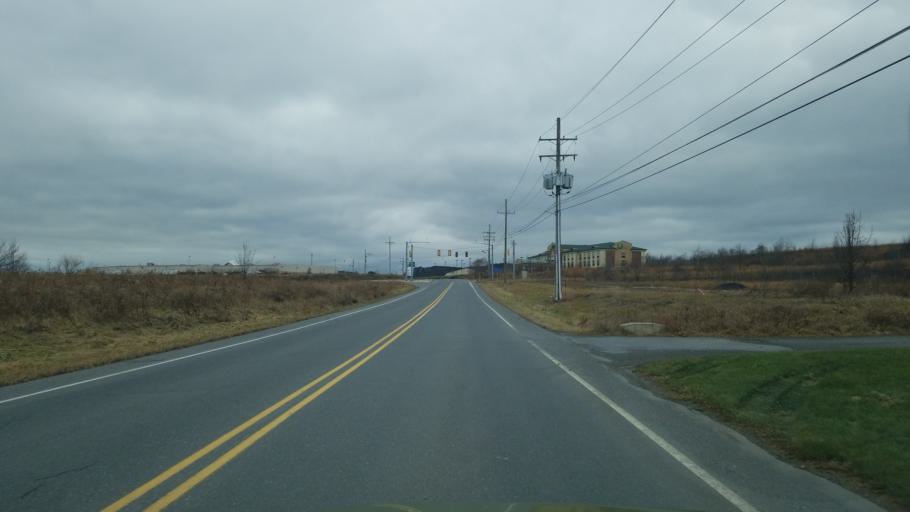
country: US
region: Pennsylvania
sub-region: Clearfield County
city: Clearfield
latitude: 41.0323
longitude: -78.3912
